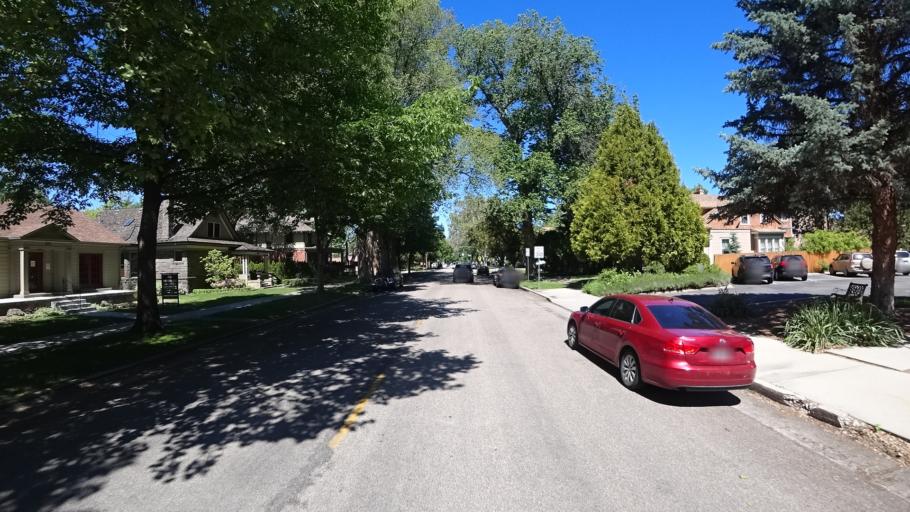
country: US
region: Idaho
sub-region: Ada County
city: Boise
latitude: 43.6199
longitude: -116.1963
